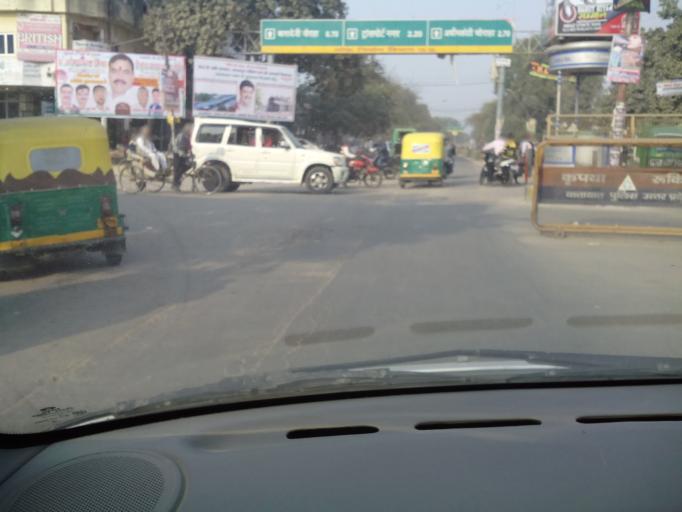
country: IN
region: Uttar Pradesh
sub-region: Kanpur
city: Kanpur
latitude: 26.4331
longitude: 80.3218
